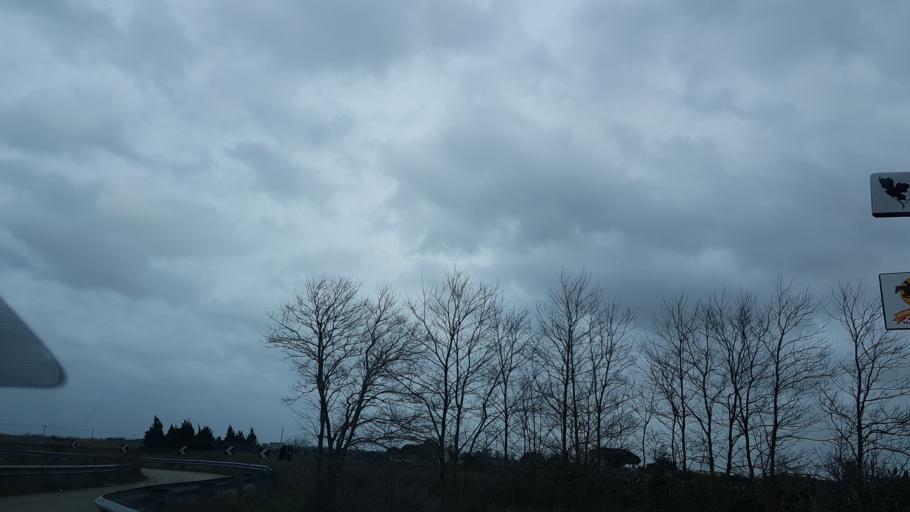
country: IT
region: Apulia
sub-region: Provincia di Brindisi
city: Brindisi
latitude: 40.6682
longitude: 17.8621
